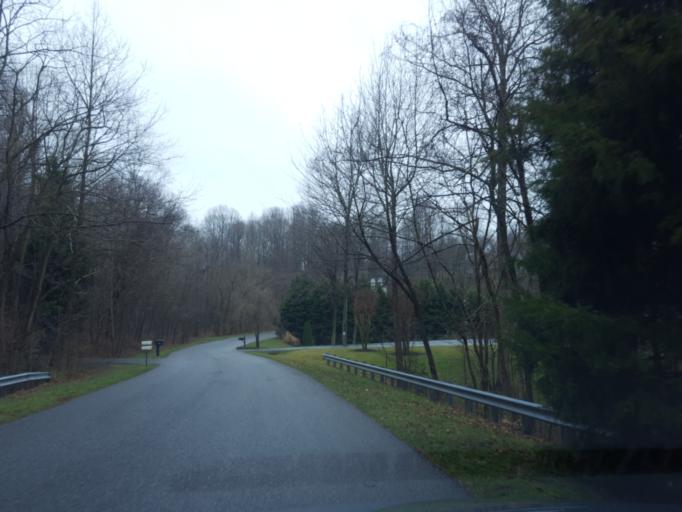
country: US
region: Maryland
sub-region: Calvert County
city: Huntingtown
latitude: 38.6068
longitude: -76.5384
